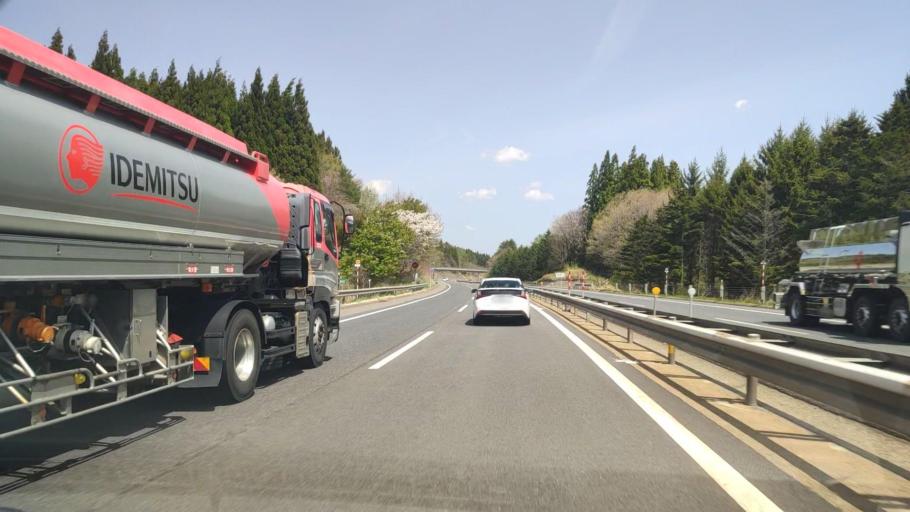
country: JP
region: Iwate
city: Ichinohe
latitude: 40.2423
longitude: 141.4010
